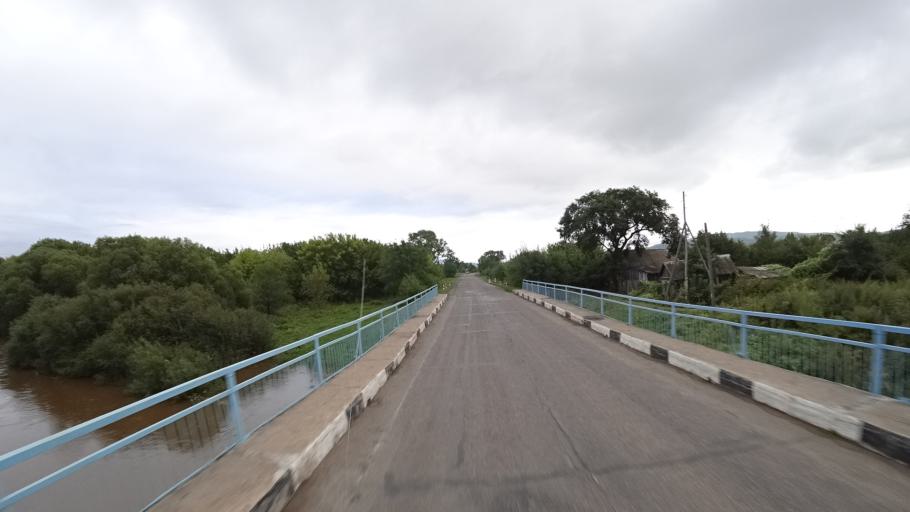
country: RU
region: Primorskiy
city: Chernigovka
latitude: 44.3530
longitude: 132.5672
